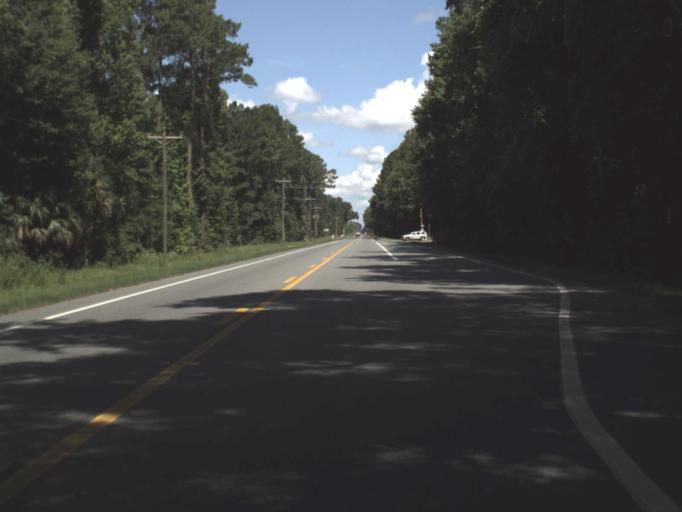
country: US
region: Florida
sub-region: Putnam County
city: Palatka
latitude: 29.6788
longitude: -81.7217
